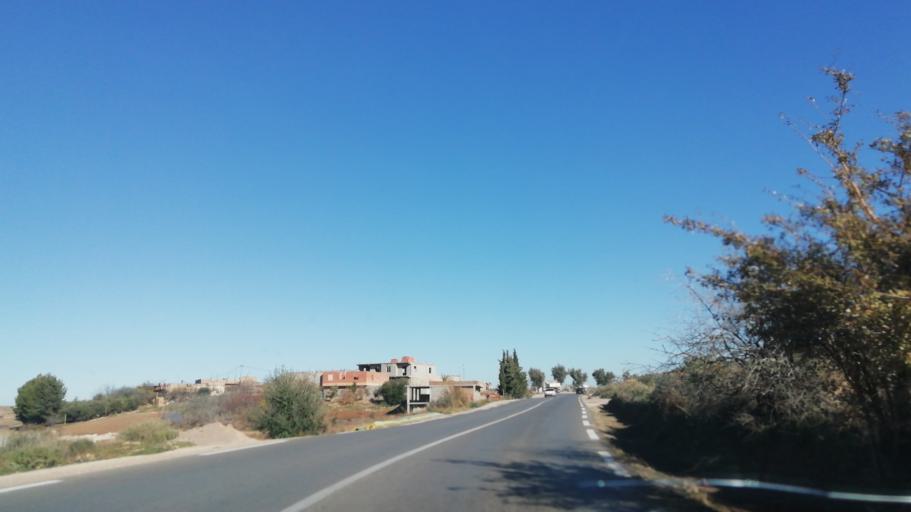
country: DZ
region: Tlemcen
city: Beni Mester
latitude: 34.8405
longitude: -1.4812
